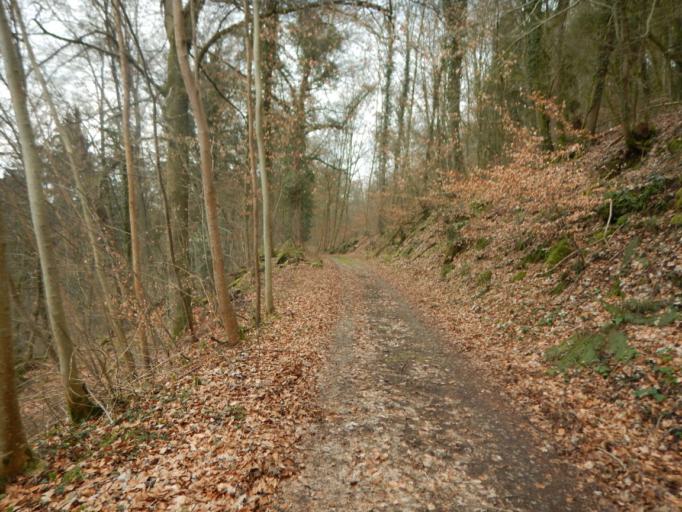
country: LU
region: Grevenmacher
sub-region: Canton d'Echternach
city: Beaufort
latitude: 49.8355
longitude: 6.3214
